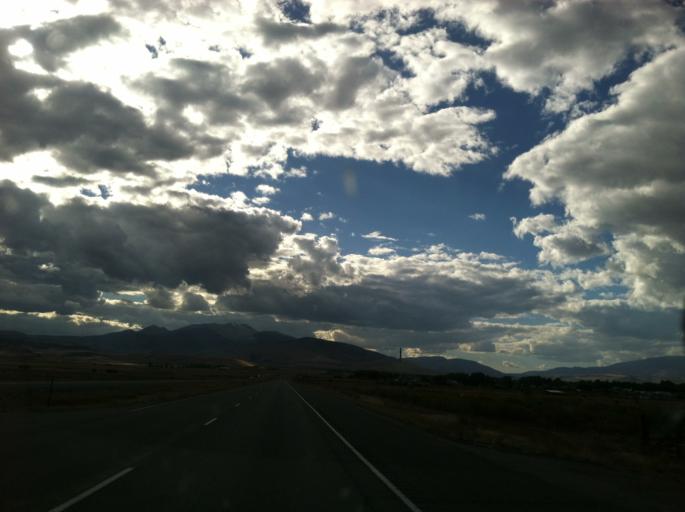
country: US
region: Montana
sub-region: Deer Lodge County
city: Warm Springs
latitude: 46.0957
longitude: -112.8102
